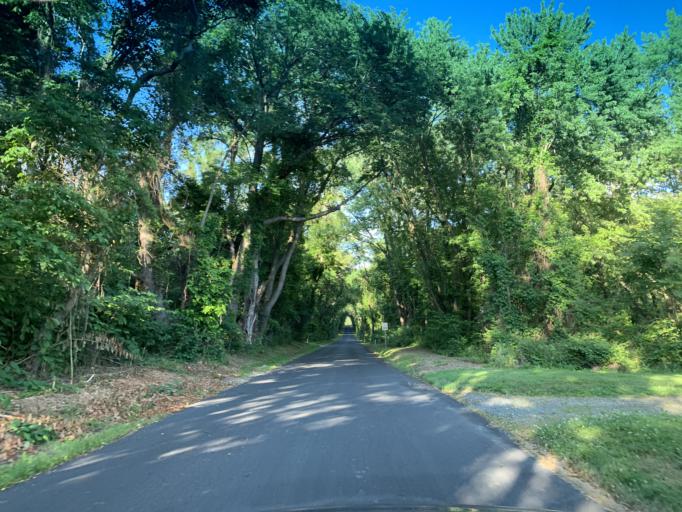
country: US
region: Maryland
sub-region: Cecil County
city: Perryville
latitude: 39.6261
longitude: -76.0975
